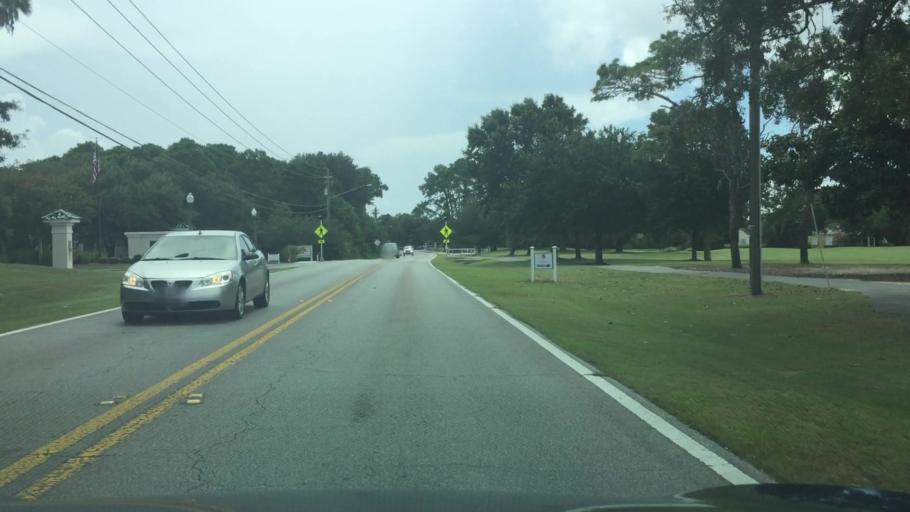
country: US
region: Florida
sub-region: Bay County
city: Upper Grand Lagoon
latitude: 30.1527
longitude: -85.7261
